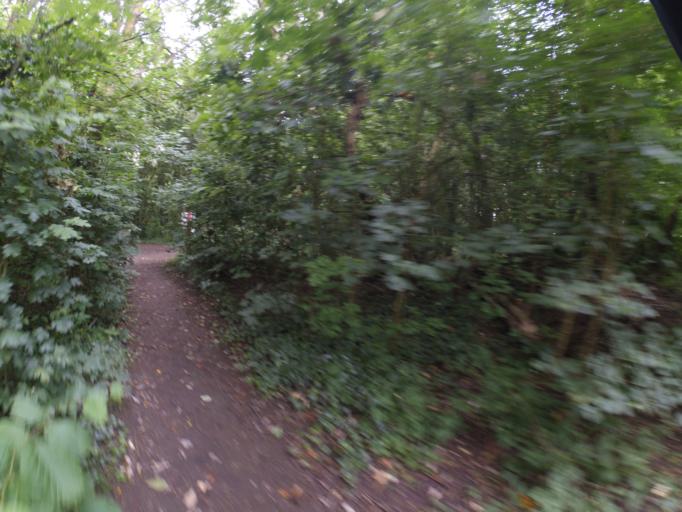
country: GB
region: England
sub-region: Warwickshire
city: Dunchurch
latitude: 52.3474
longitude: -1.2779
